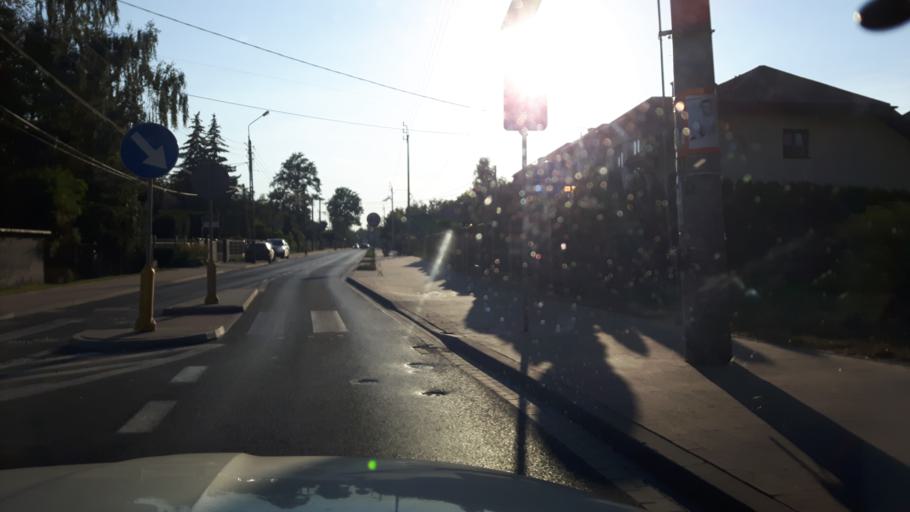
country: PL
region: Masovian Voivodeship
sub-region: Powiat wolominski
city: Kobylka
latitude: 52.3413
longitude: 21.2085
